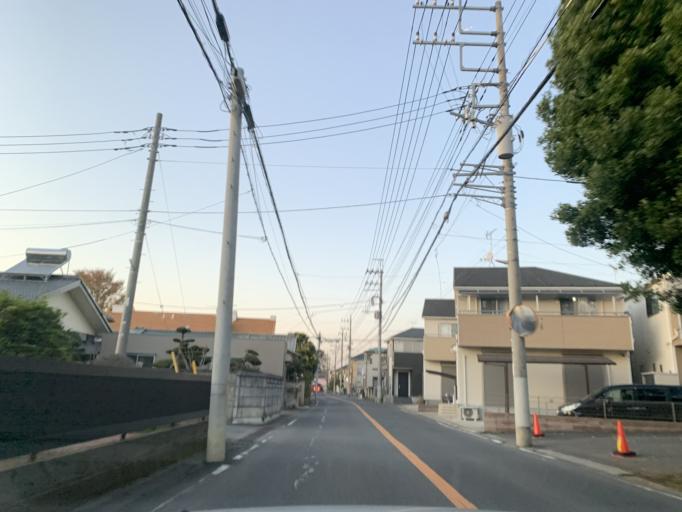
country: JP
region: Chiba
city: Nagareyama
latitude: 35.9025
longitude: 139.9060
